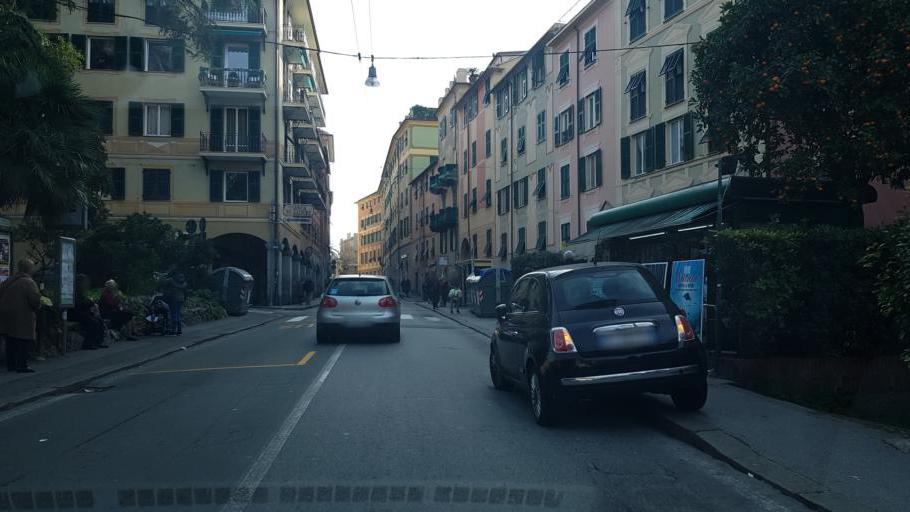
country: IT
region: Liguria
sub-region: Provincia di Genova
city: Bogliasco
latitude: 44.3845
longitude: 9.0353
